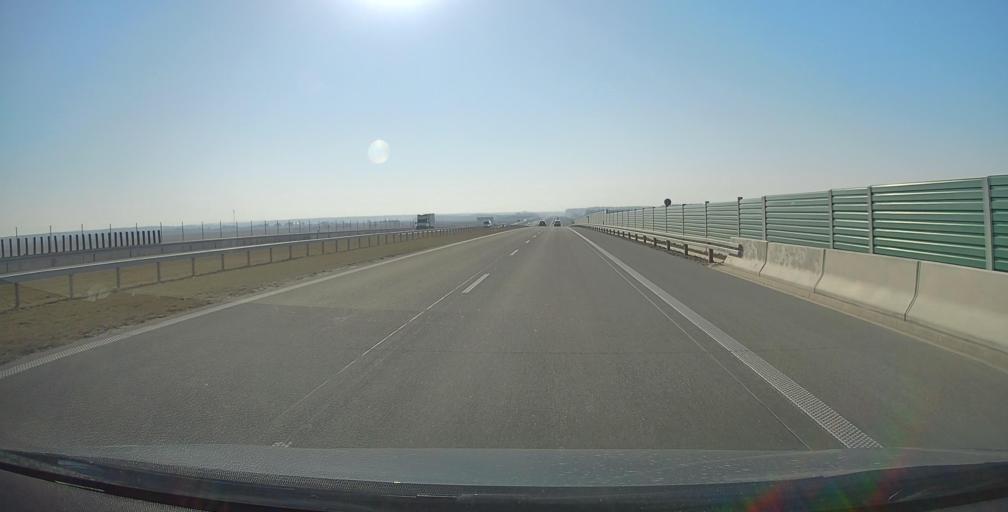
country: PL
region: Masovian Voivodeship
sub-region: Powiat garwolinski
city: Pilawa
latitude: 52.0164
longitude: 21.5183
